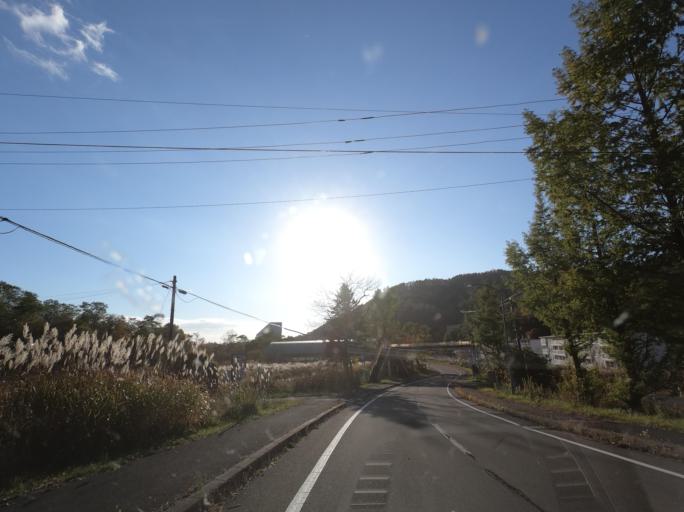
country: JP
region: Hokkaido
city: Iwamizawa
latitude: 43.0544
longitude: 141.9730
